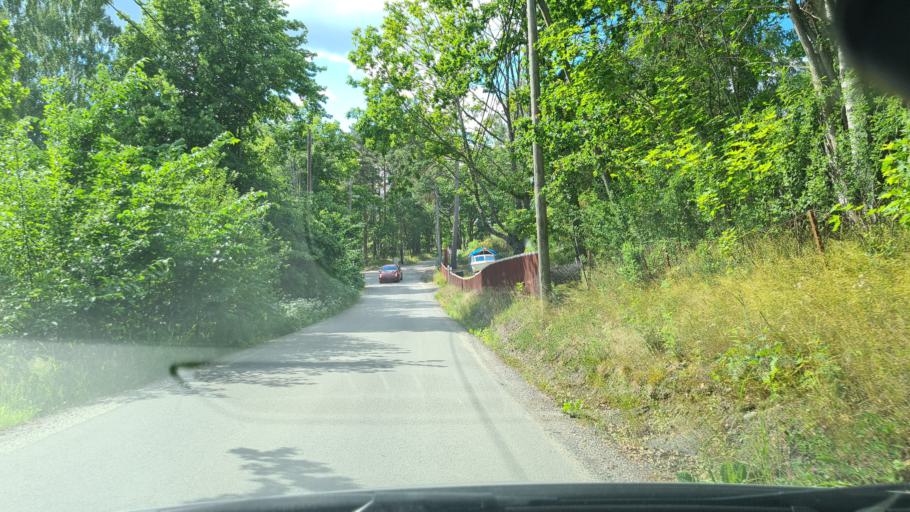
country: SE
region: Stockholm
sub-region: Vaxholms Kommun
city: Vaxholm
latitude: 59.4111
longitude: 18.3761
